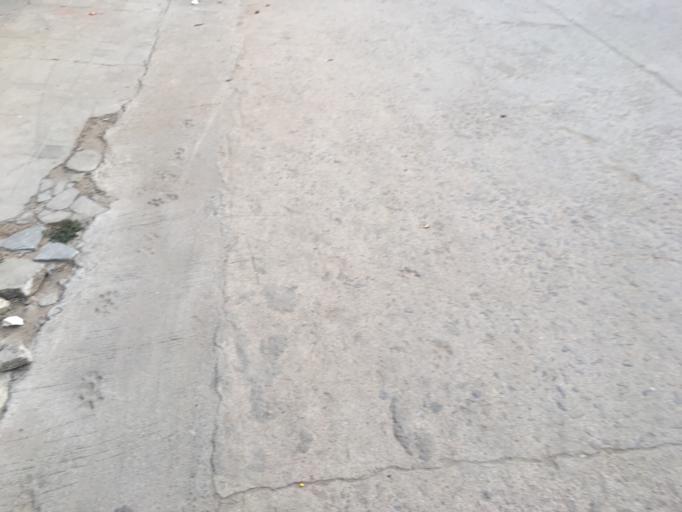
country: IN
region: Telangana
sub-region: Rangareddi
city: Gaddi Annaram
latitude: 17.3696
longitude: 78.5258
